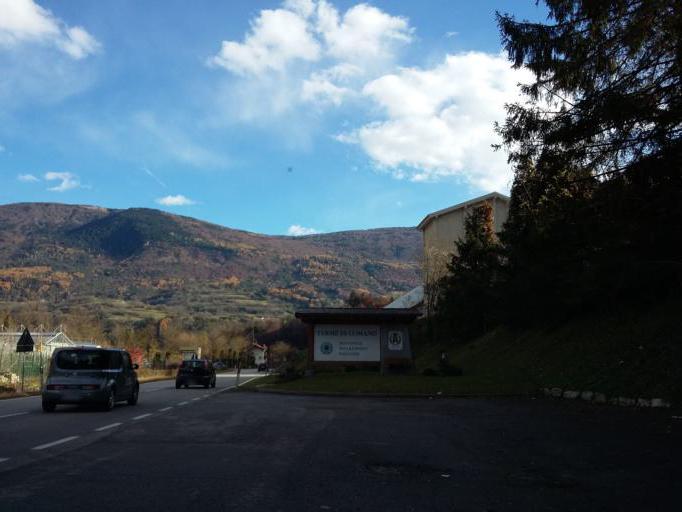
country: IT
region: Trentino-Alto Adige
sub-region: Provincia di Trento
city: Stenico
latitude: 46.0383
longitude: 10.8575
